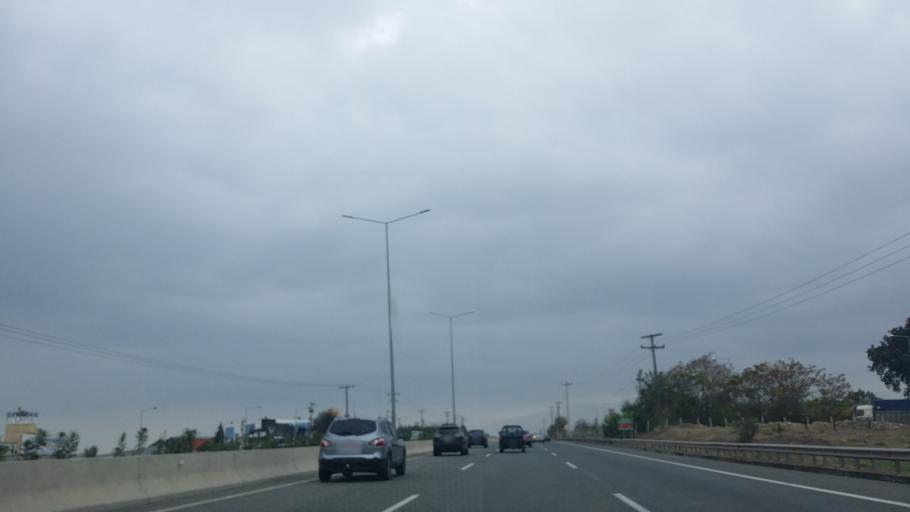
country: GR
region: Central Greece
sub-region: Nomos Voiotias
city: Oinofyta
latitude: 38.3268
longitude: 23.6105
